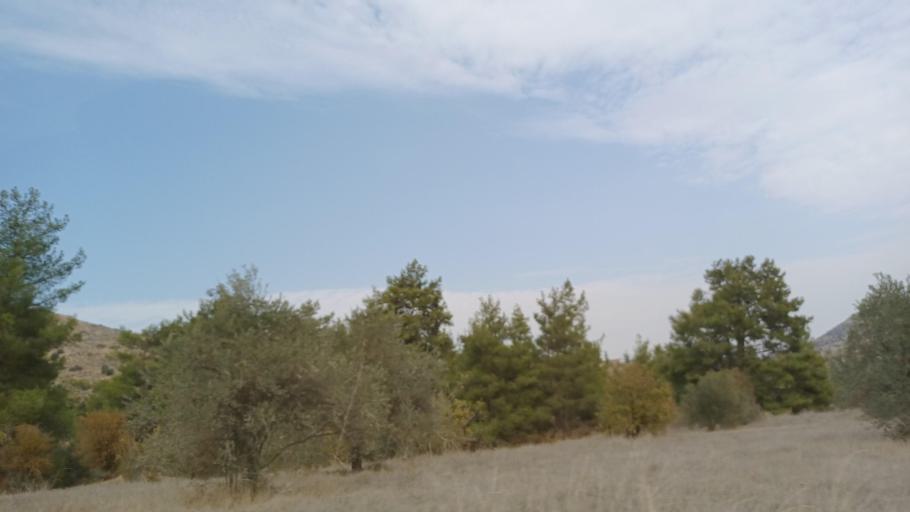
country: CY
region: Lefkosia
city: Klirou
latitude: 35.0405
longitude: 33.1151
